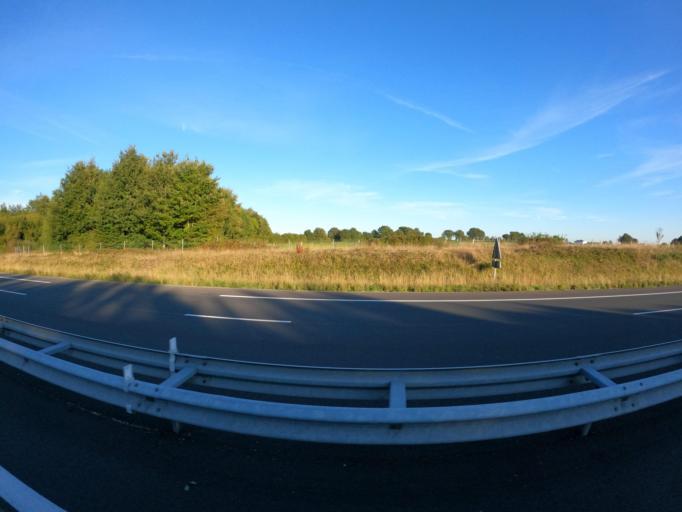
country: FR
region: Pays de la Loire
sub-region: Departement de la Vendee
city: Saint-Fulgent
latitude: 46.8560
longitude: -1.1434
